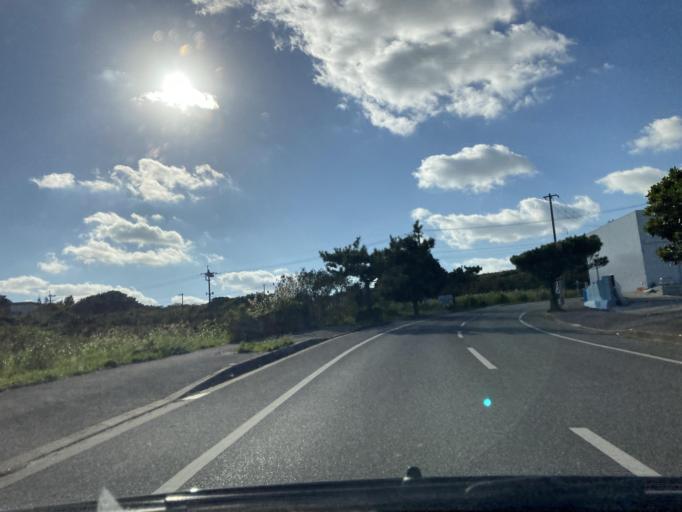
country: JP
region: Okinawa
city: Katsuren-haebaru
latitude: 26.3049
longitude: 127.9196
